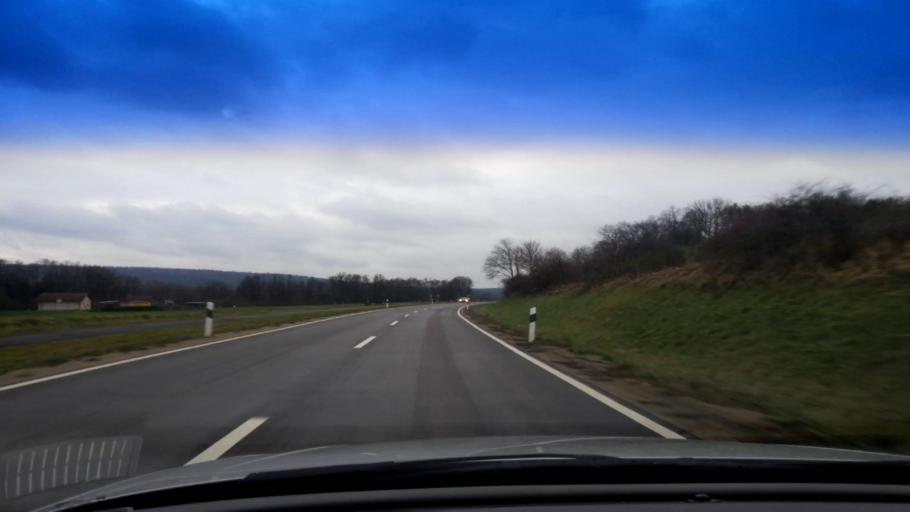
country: DE
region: Bavaria
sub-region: Upper Franconia
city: Pettstadt
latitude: 49.8341
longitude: 10.9247
